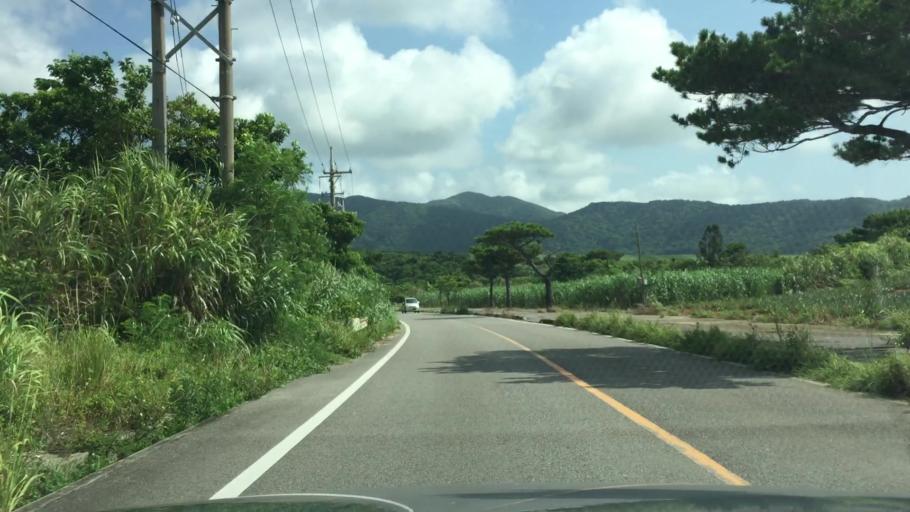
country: JP
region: Okinawa
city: Ishigaki
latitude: 24.4133
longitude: 124.2147
